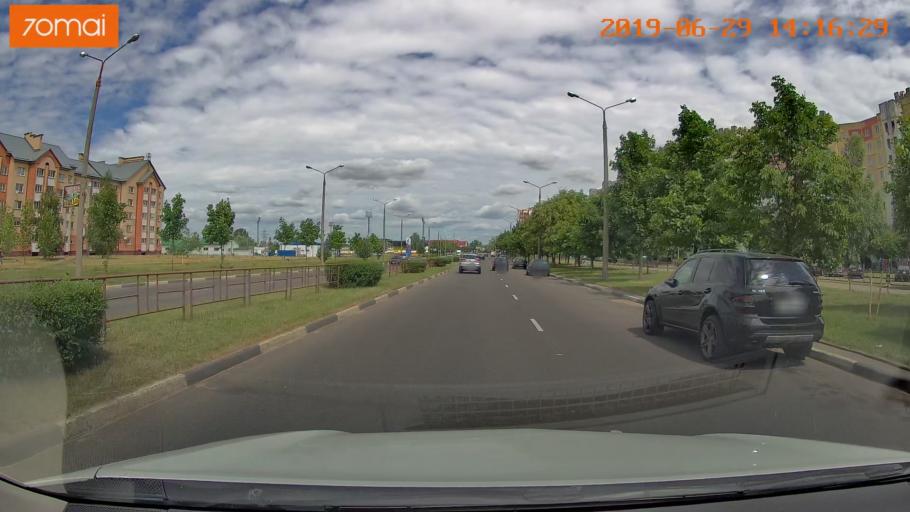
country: BY
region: Minsk
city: Salihorsk
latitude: 52.7955
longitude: 27.5326
